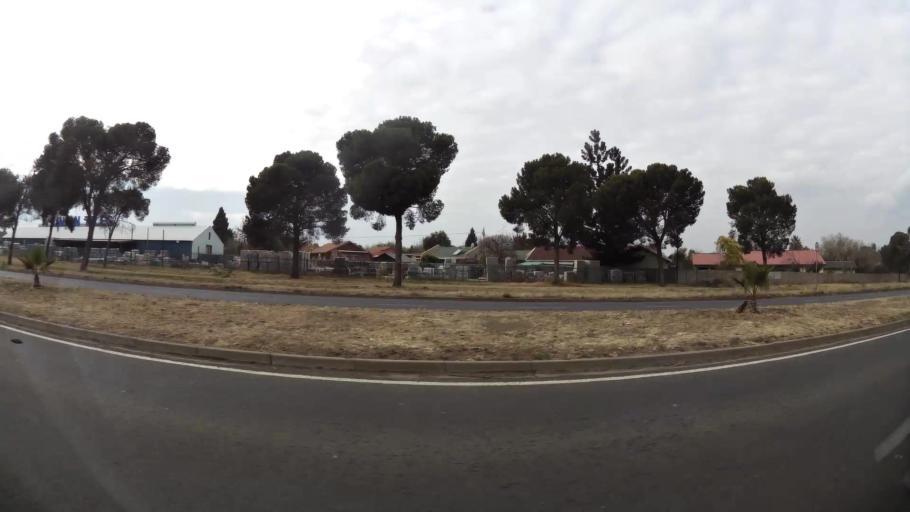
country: ZA
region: Orange Free State
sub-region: Mangaung Metropolitan Municipality
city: Bloemfontein
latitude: -29.1576
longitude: 26.1863
